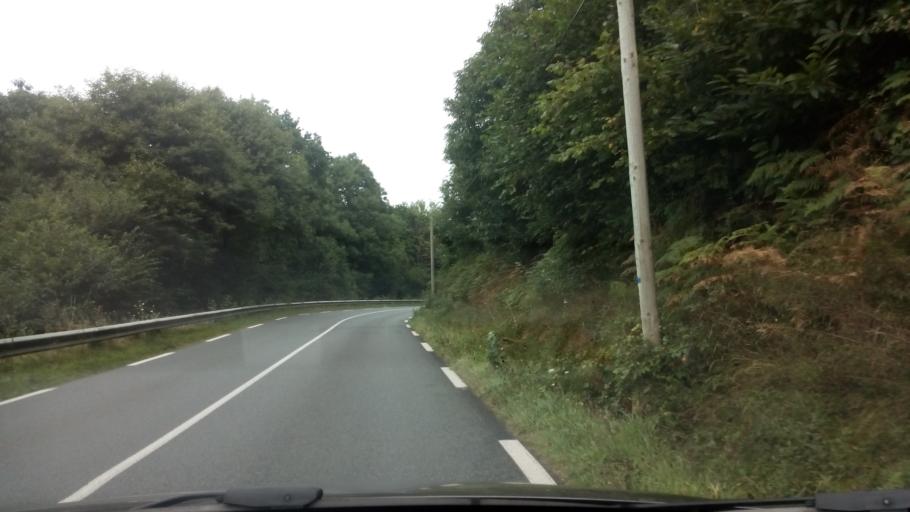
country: FR
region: Brittany
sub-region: Departement des Cotes-d'Armor
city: Locquemeau
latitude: 48.6866
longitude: -3.5613
